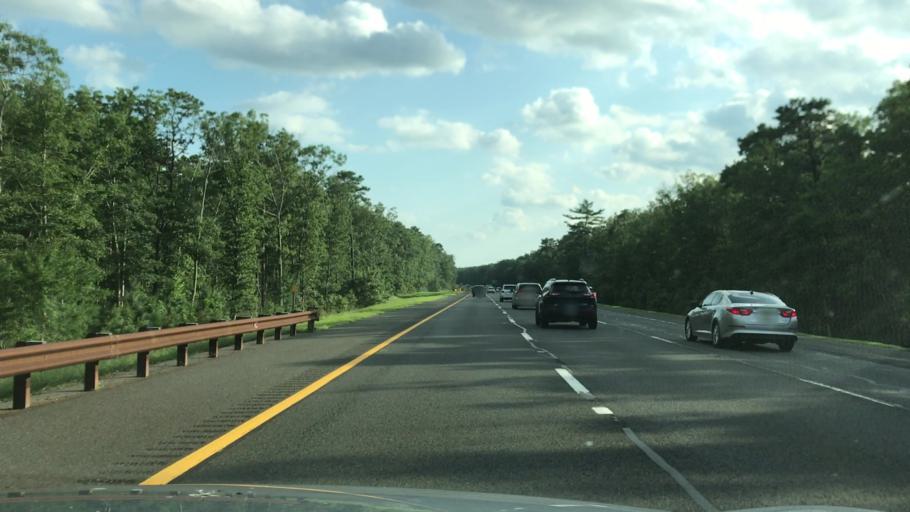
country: US
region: New Jersey
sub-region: Ocean County
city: Ocean Acres
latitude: 39.7350
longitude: -74.2626
